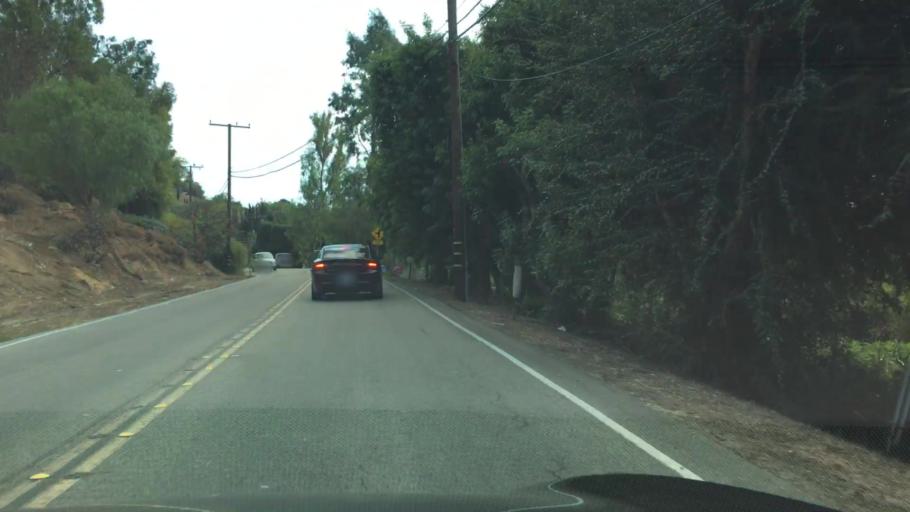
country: US
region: California
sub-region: Los Angeles County
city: La Habra Heights
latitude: 33.9633
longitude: -117.9590
